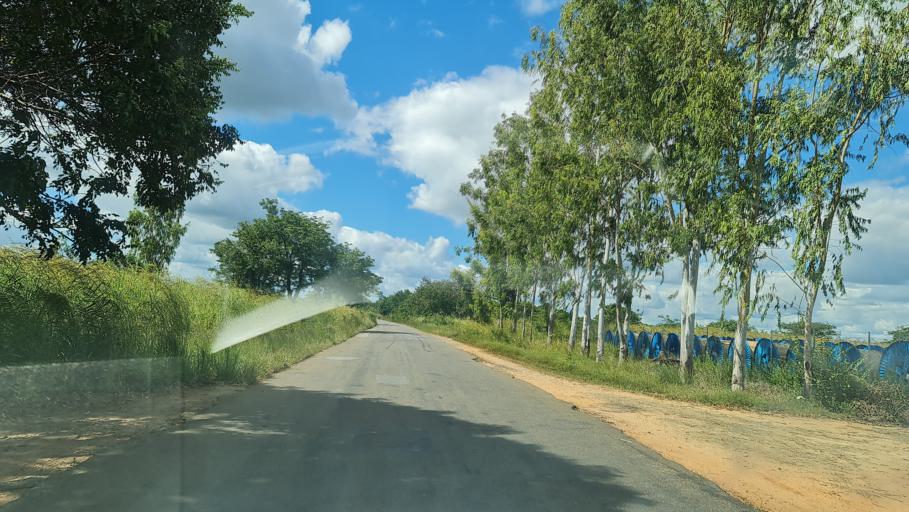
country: MZ
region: Zambezia
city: Quelimane
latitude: -17.5092
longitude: 36.2342
